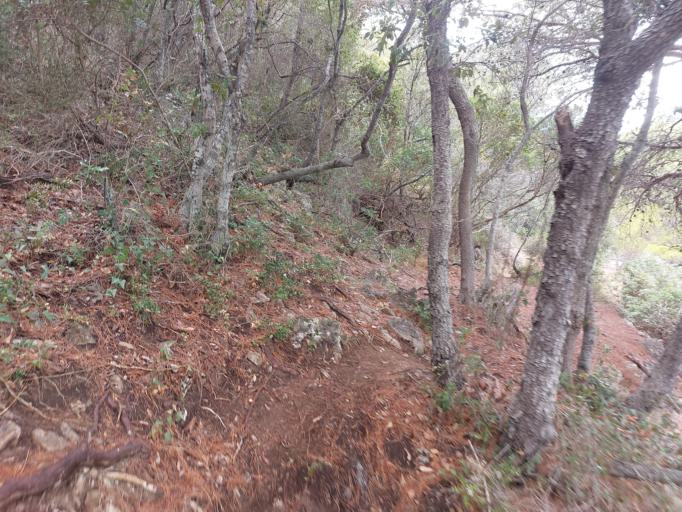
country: HR
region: Dubrovacko-Neretvanska
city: Smokvica
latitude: 42.7630
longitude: 16.8138
